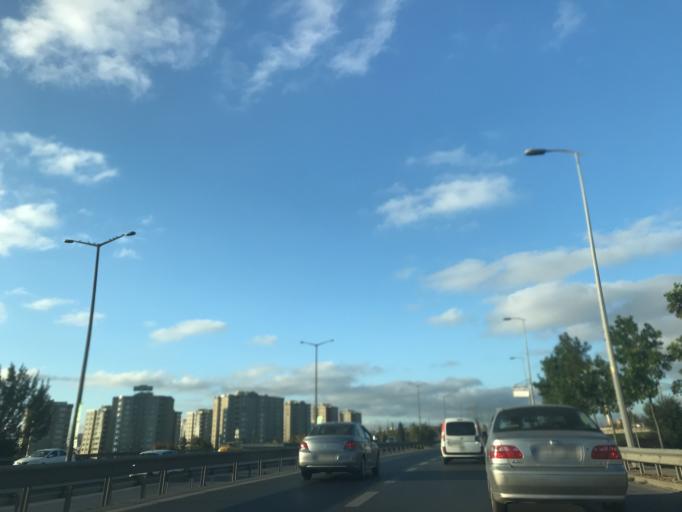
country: TR
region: Istanbul
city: Esenler
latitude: 41.0443
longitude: 28.8850
